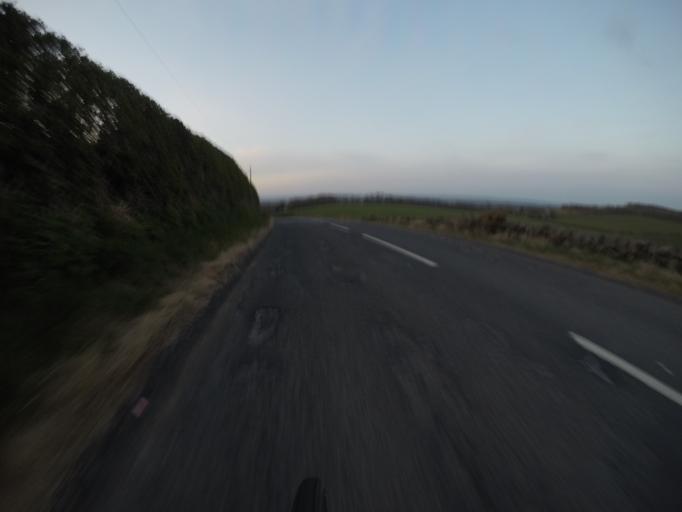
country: GB
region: Scotland
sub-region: South Ayrshire
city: Dundonald
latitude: 55.5660
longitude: -4.6016
